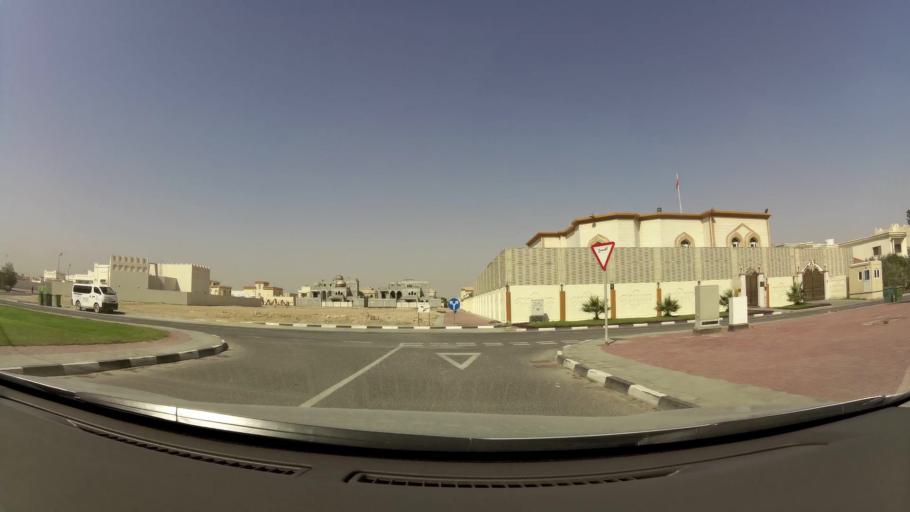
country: QA
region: Baladiyat ad Dawhah
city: Doha
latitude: 25.3590
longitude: 51.5088
